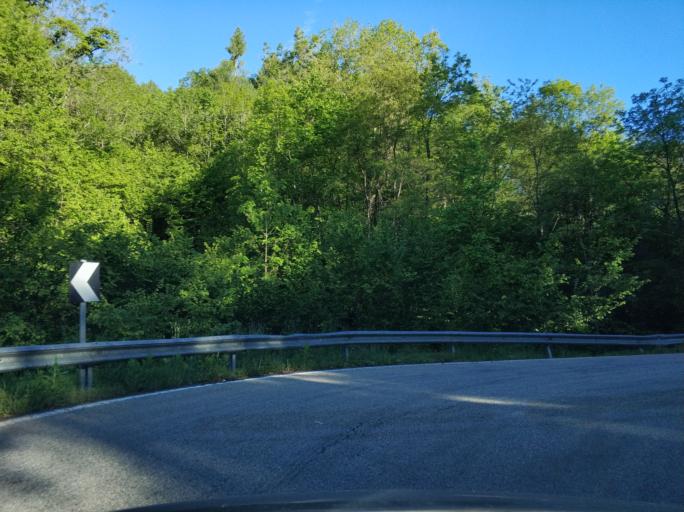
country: IT
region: Piedmont
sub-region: Provincia di Torino
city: Coassolo
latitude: 45.2917
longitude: 7.4695
